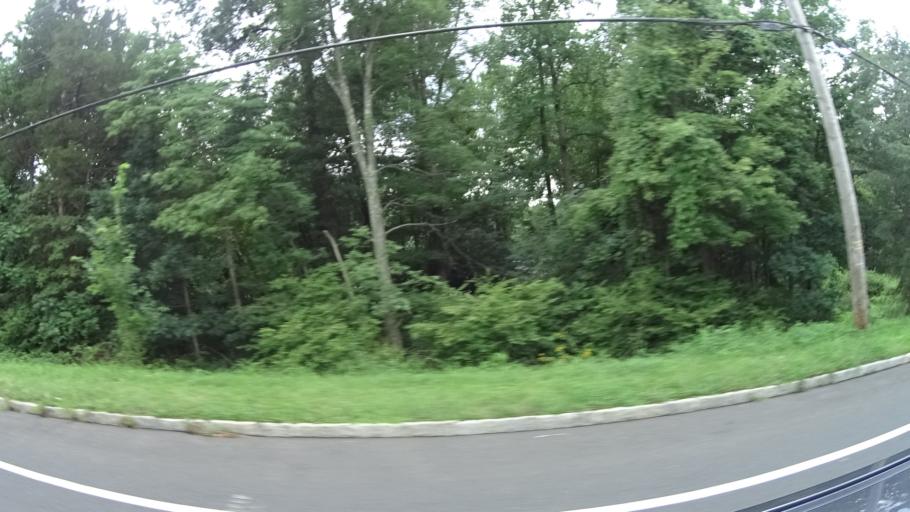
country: US
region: New Jersey
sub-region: Somerset County
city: Warren Township
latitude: 40.6434
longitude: -74.5168
